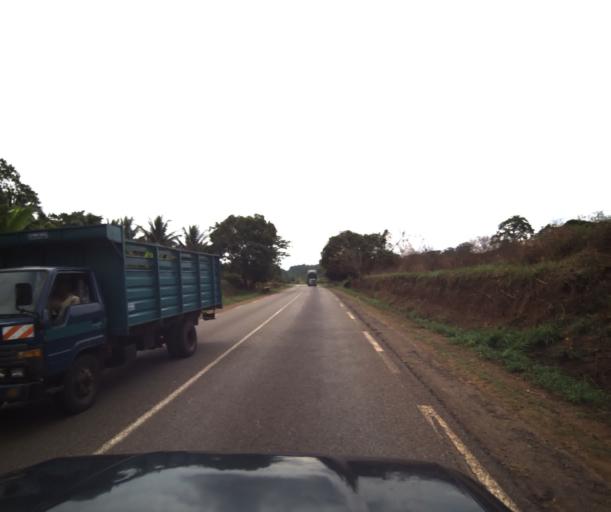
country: CM
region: Littoral
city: Edea
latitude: 3.8357
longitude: 10.4288
